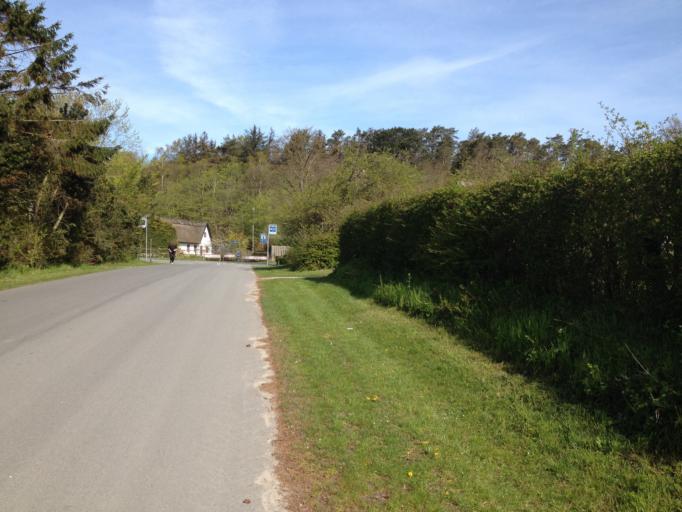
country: DK
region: Capital Region
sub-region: Halsnaes Kommune
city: Hundested
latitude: 55.9469
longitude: 11.8999
